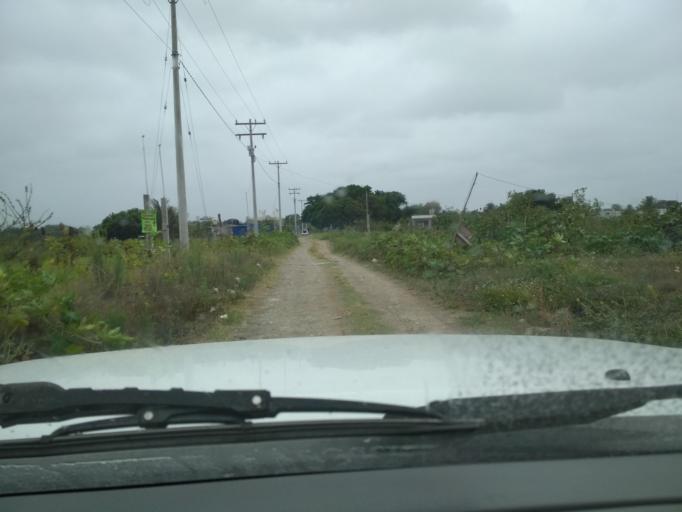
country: MX
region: Veracruz
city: Paso del Toro
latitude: 19.0421
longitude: -96.1322
